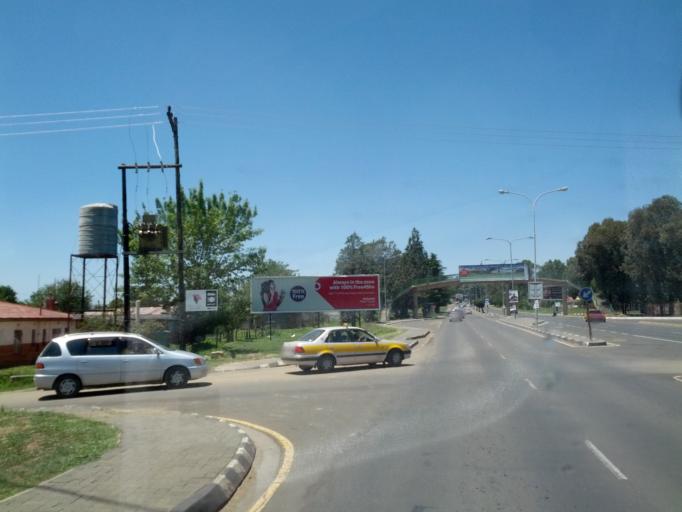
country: LS
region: Maseru
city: Maseru
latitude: -29.3014
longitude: 27.4620
